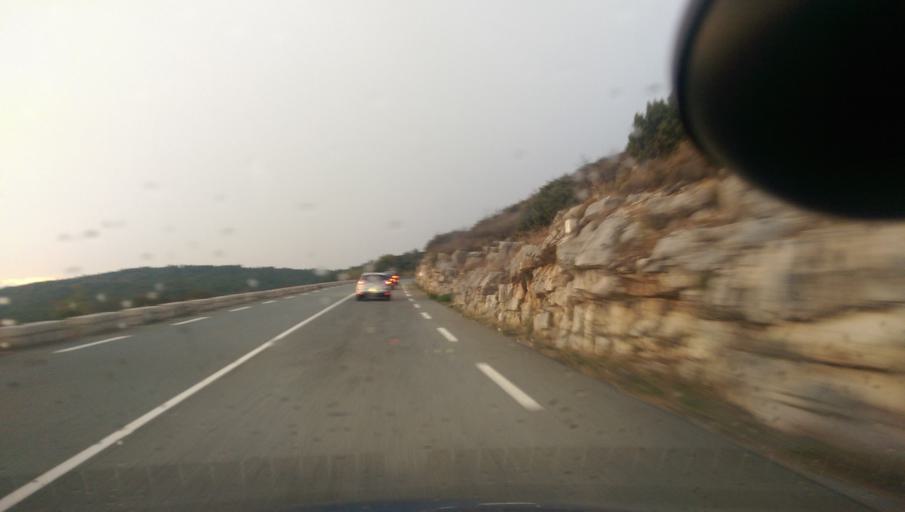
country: FR
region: Provence-Alpes-Cote d'Azur
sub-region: Departement des Alpes-Maritimes
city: Grasse
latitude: 43.6783
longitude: 6.8980
